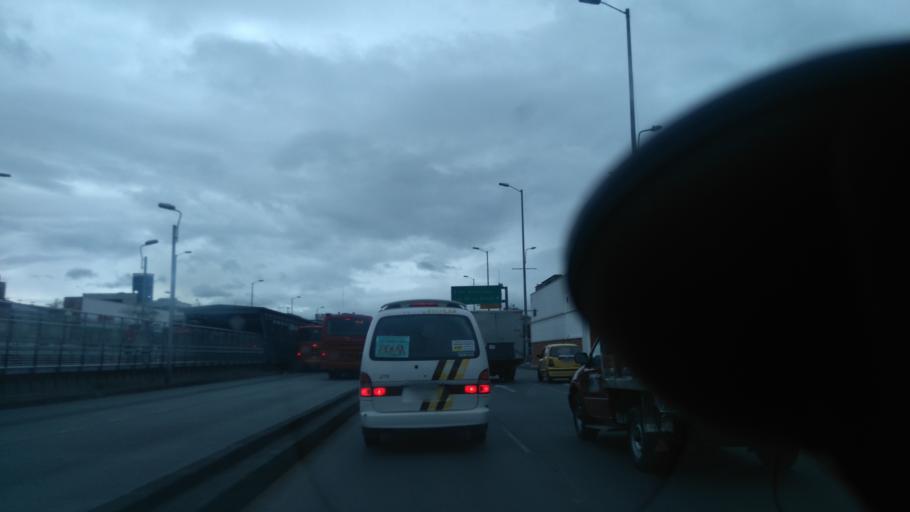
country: CO
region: Bogota D.C.
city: Bogota
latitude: 4.6226
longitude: -74.1011
